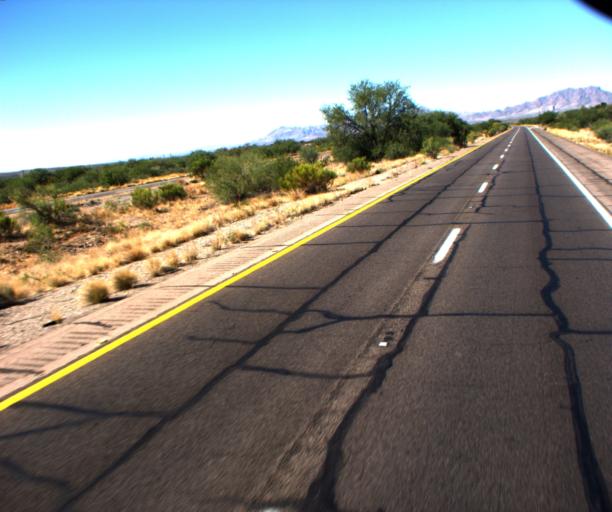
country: US
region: Arizona
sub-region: Pima County
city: Arivaca Junction
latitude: 31.7376
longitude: -111.0518
